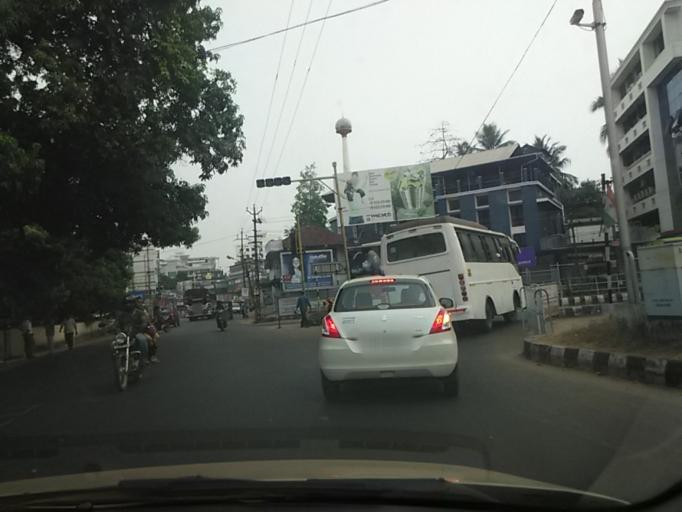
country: IN
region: Kerala
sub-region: Kozhikode
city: Kozhikode
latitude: 11.2711
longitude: 75.7758
